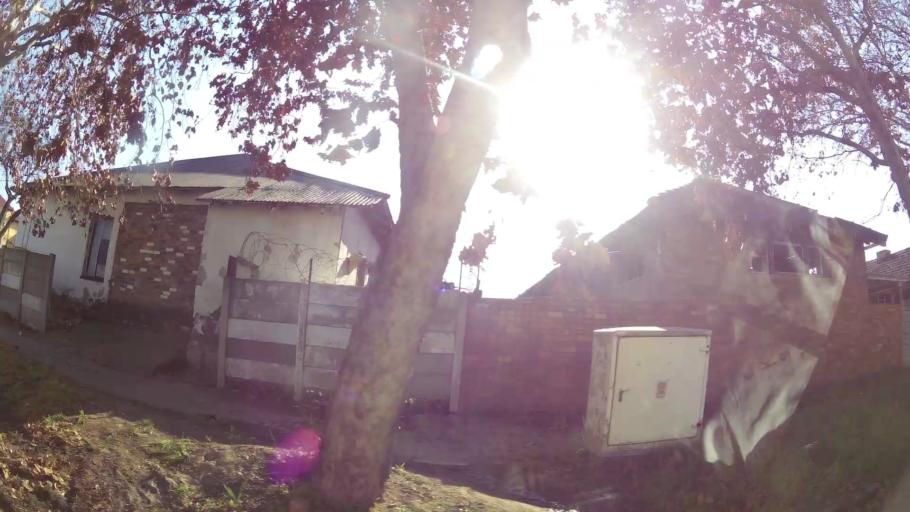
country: ZA
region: Gauteng
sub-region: Ekurhuleni Metropolitan Municipality
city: Boksburg
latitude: -26.2208
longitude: 28.2384
